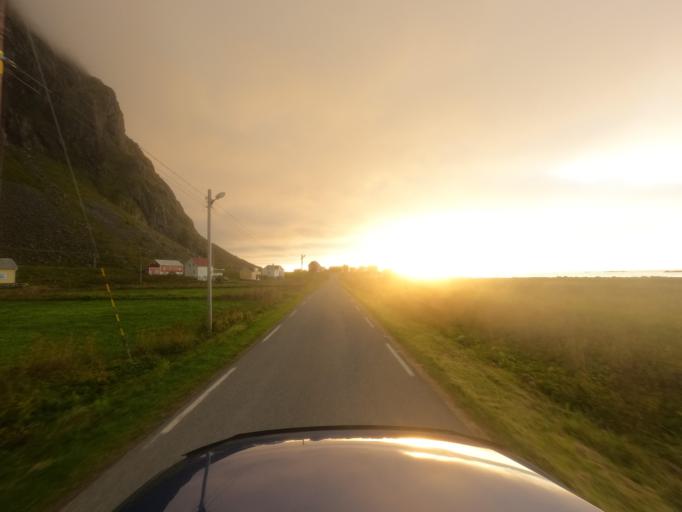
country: NO
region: Nordland
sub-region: Vestvagoy
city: Evjen
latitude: 68.3082
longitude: 13.6799
